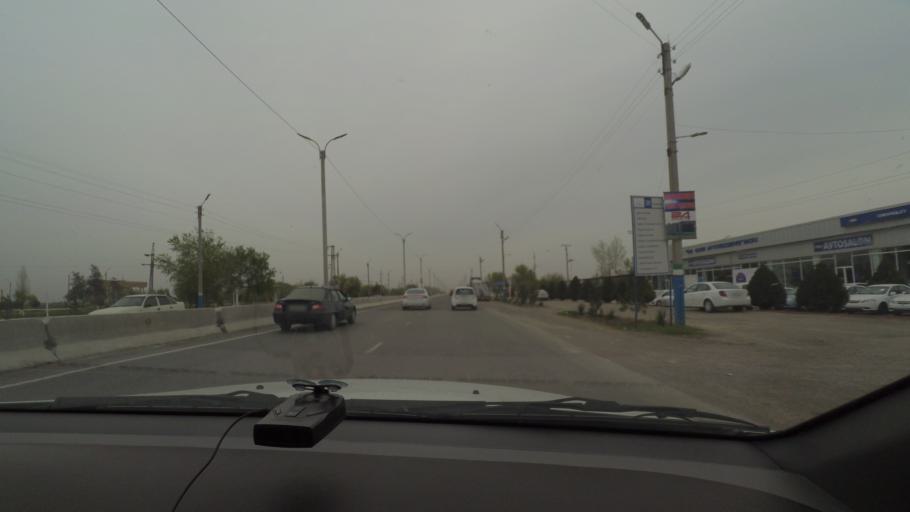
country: KZ
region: Ongtustik Qazaqstan
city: Myrzakent
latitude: 40.5419
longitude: 68.4178
